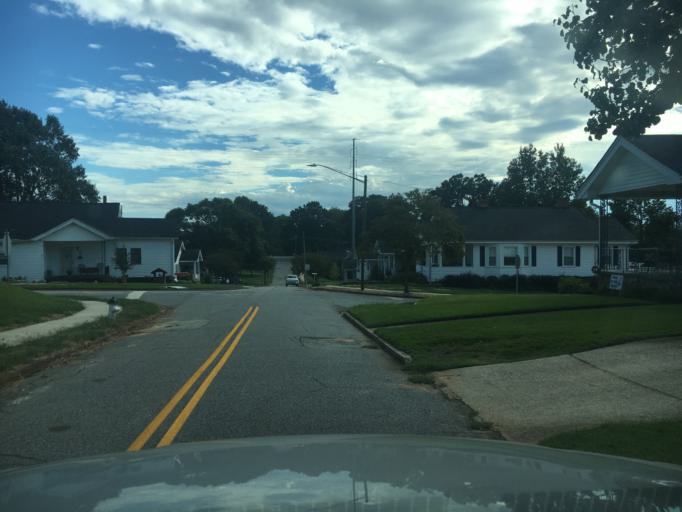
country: US
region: South Carolina
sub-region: Spartanburg County
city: Lyman
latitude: 34.9504
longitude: -82.1263
